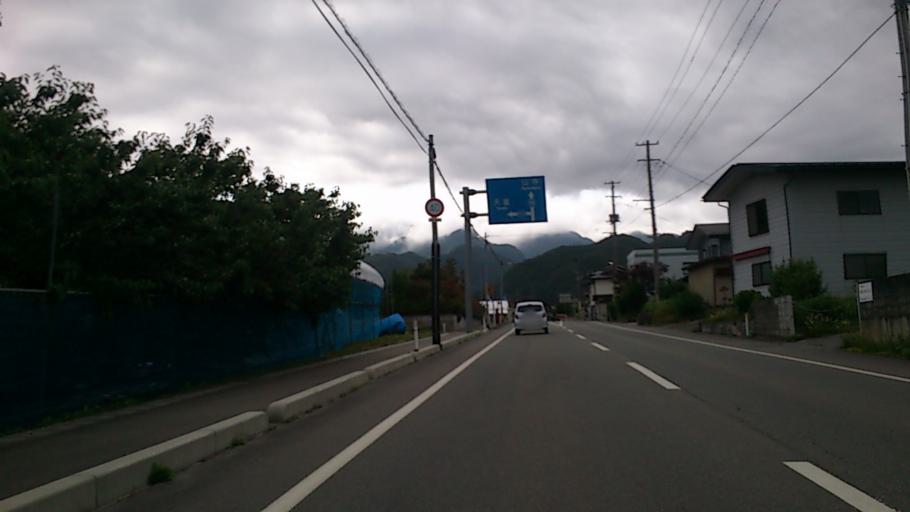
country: JP
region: Yamagata
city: Tendo
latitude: 38.3125
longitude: 140.4148
